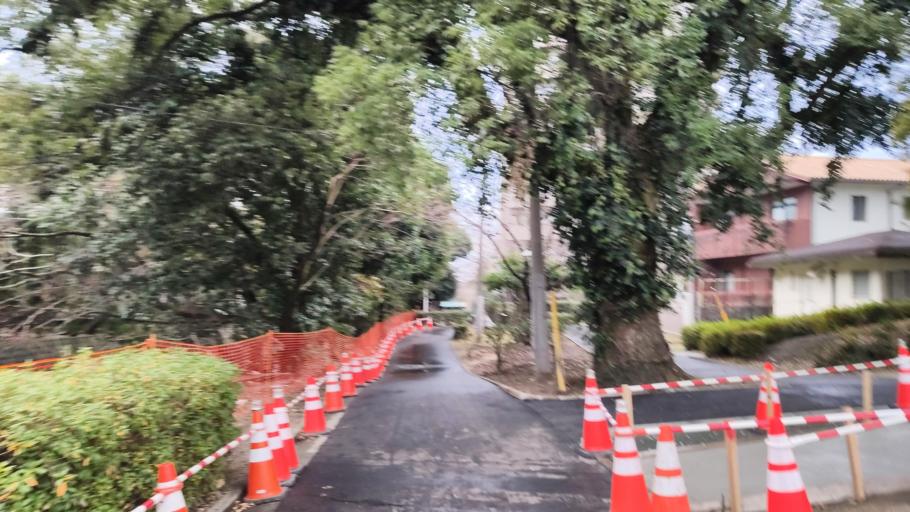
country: JP
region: Kumamoto
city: Kumamoto
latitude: 32.7876
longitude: 130.7346
